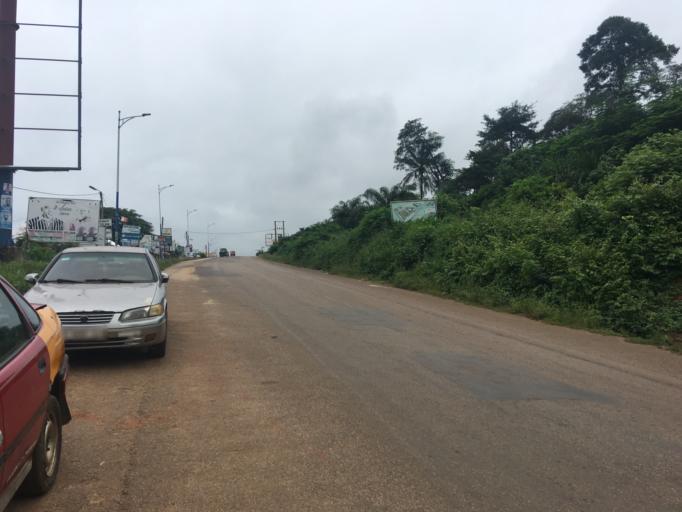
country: GH
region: Western
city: Bibiani
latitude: 6.8062
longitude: -2.5115
